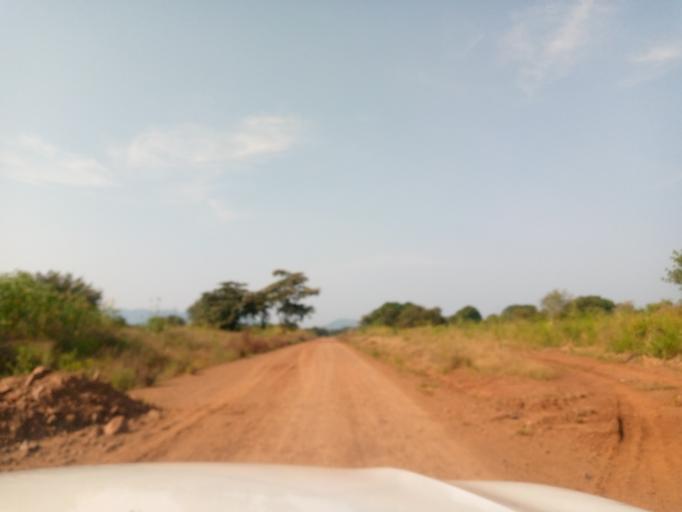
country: ET
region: Oromiya
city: Mendi
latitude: 10.1420
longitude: 34.9488
